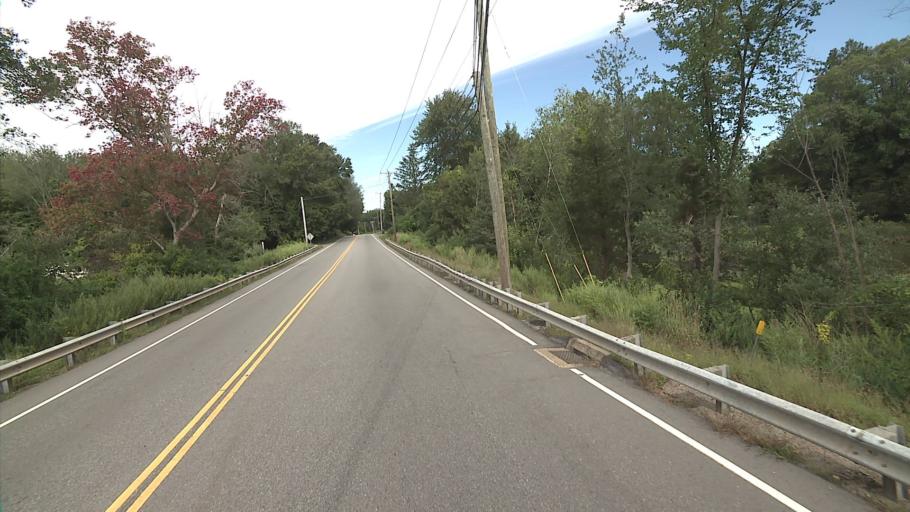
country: US
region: Connecticut
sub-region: Windham County
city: South Windham
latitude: 41.6195
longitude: -72.1515
